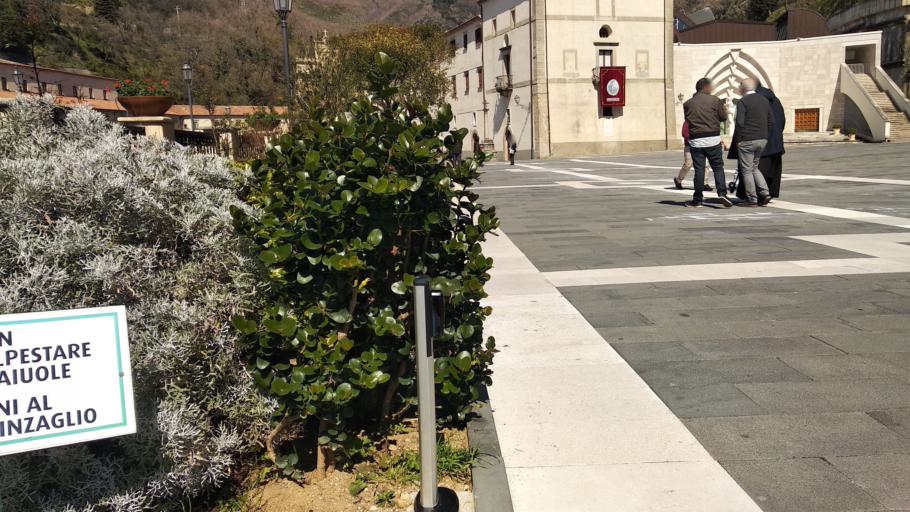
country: IT
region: Calabria
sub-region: Provincia di Cosenza
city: Paola
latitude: 39.3681
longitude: 16.0448
